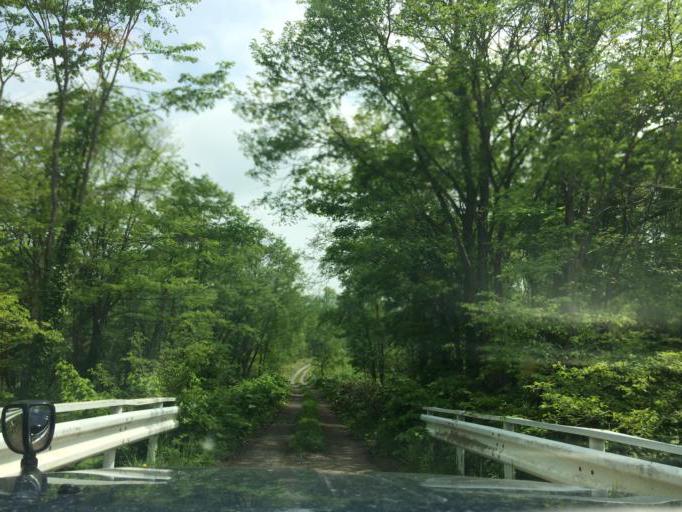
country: JP
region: Hokkaido
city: Niseko Town
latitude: 42.6748
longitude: 140.6006
